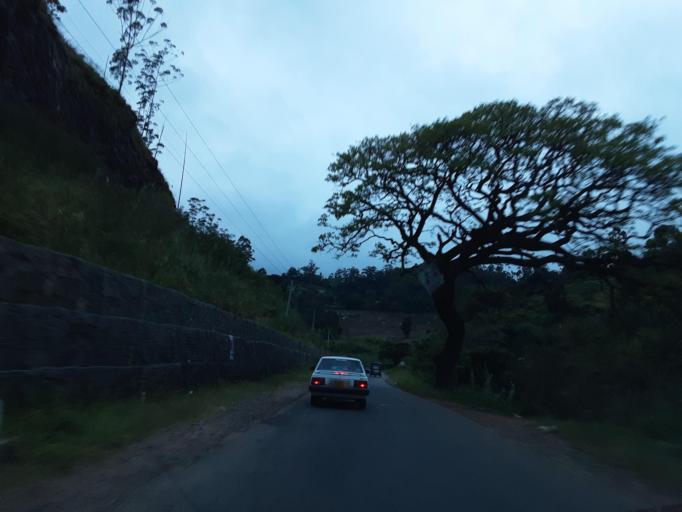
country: LK
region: Uva
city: Haputale
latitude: 6.9076
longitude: 80.9257
